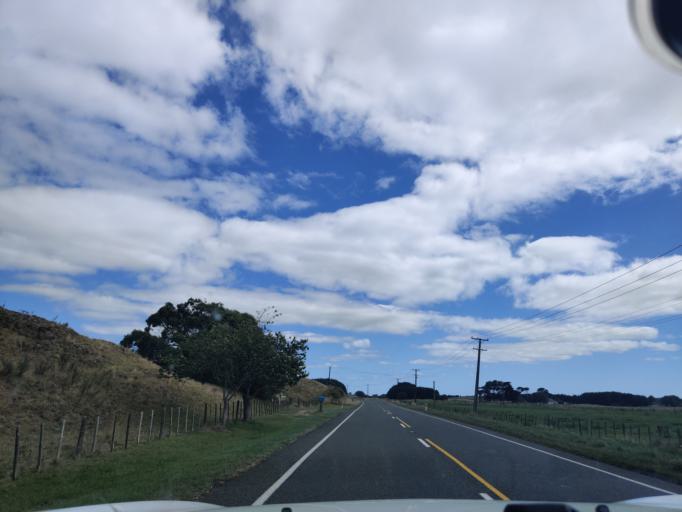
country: NZ
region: Manawatu-Wanganui
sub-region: Horowhenua District
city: Foxton
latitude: -40.4068
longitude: 175.3749
